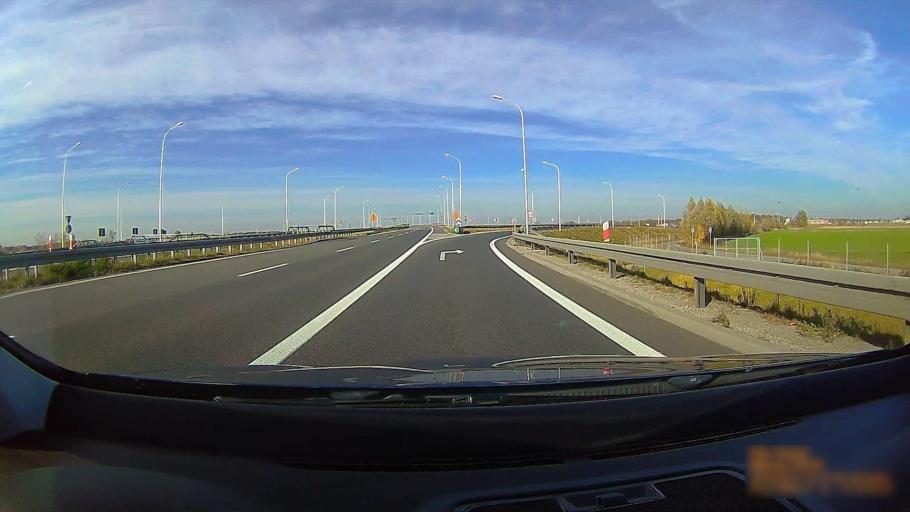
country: PL
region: Greater Poland Voivodeship
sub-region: Powiat ostrowski
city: Ostrow Wielkopolski
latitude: 51.6627
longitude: 17.8587
